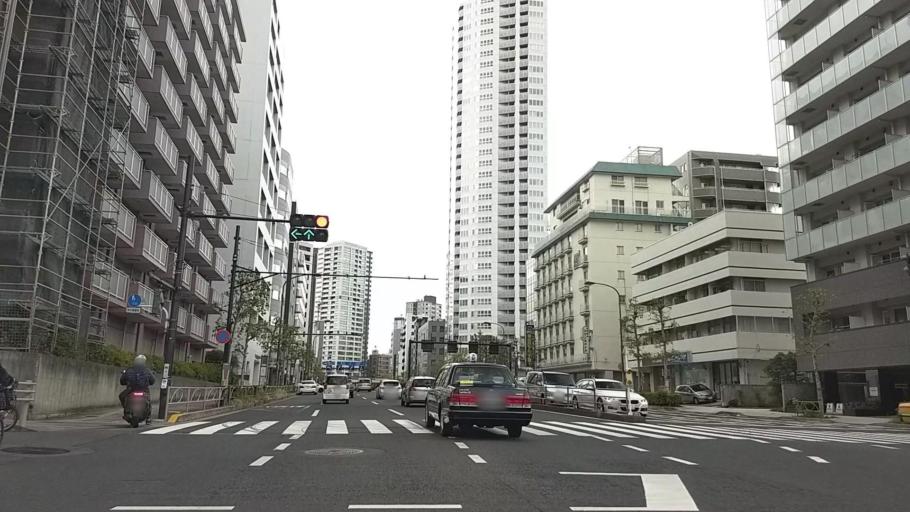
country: JP
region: Tokyo
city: Tokyo
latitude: 35.6359
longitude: 139.7315
